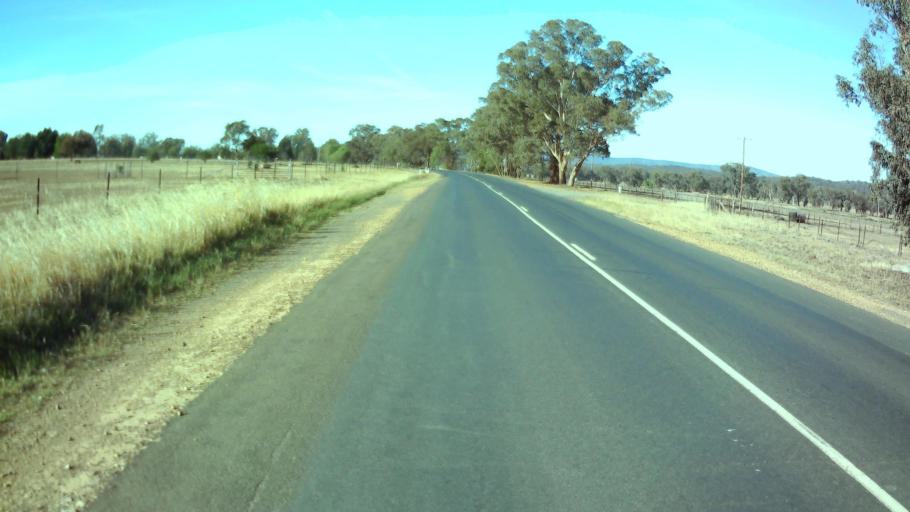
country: AU
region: New South Wales
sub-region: Weddin
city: Grenfell
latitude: -33.9064
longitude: 148.1471
